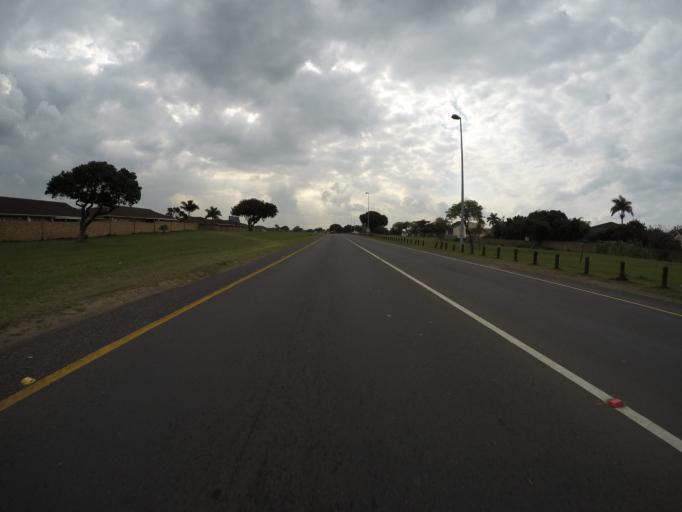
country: ZA
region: KwaZulu-Natal
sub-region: uThungulu District Municipality
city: Richards Bay
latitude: -28.7562
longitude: 32.0581
